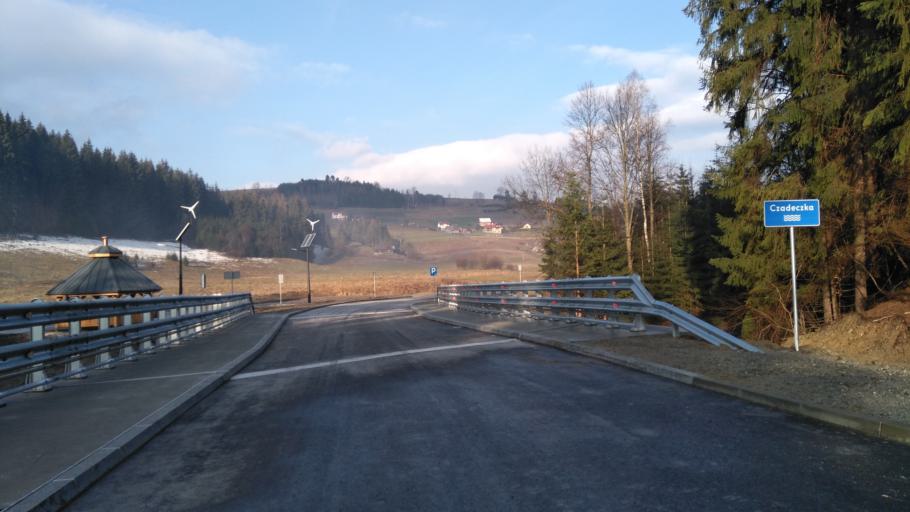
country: PL
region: Silesian Voivodeship
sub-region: Powiat cieszynski
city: Jaworzynka
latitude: 49.5186
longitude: 18.8758
